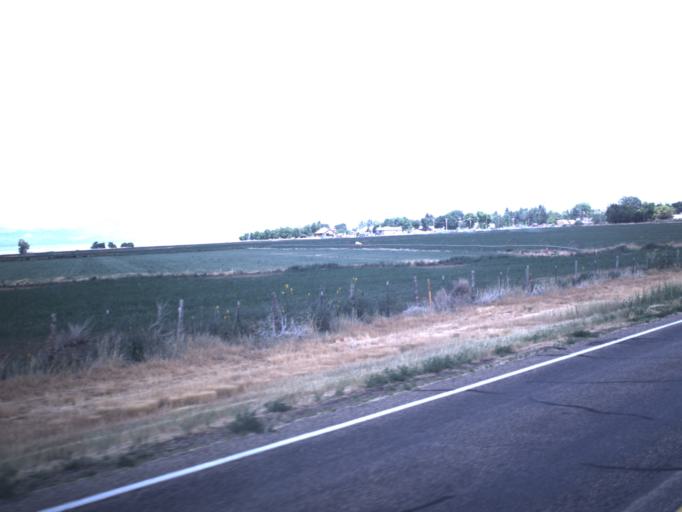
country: US
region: Utah
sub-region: Iron County
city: Parowan
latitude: 37.8774
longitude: -112.7831
